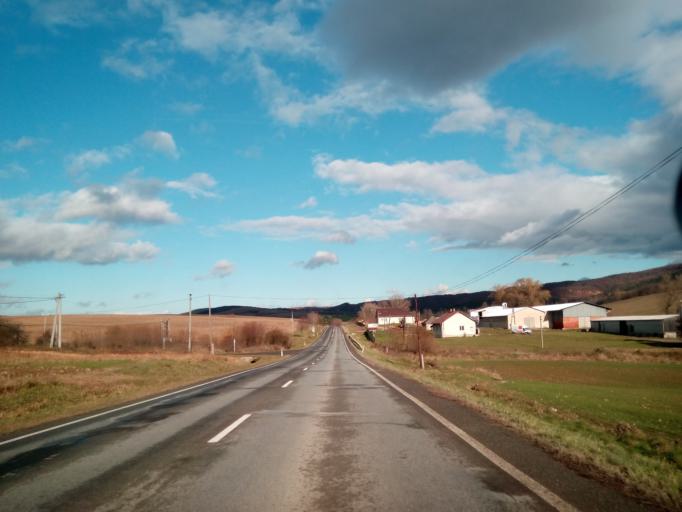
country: SK
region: Presovsky
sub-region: Okres Bardejov
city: Bardejov
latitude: 49.1905
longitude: 21.3091
